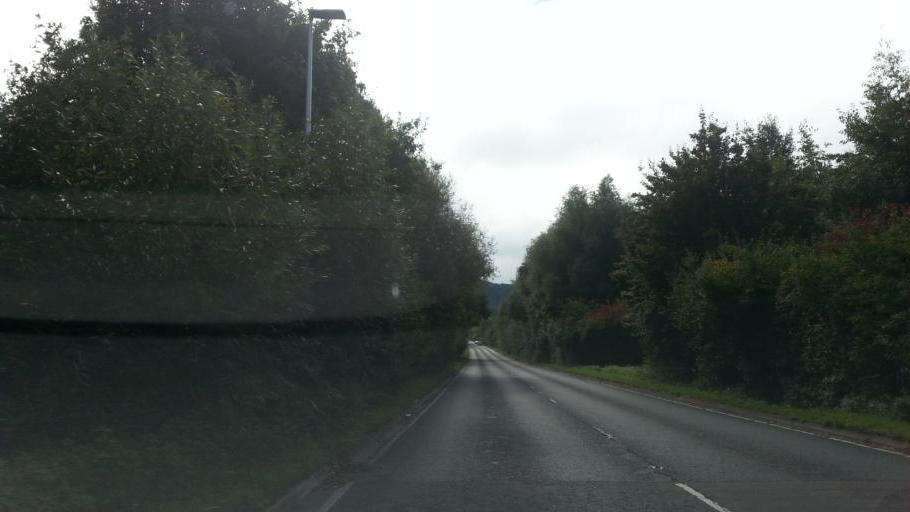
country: GB
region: England
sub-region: Herefordshire
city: Ross on Wye
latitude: 51.9199
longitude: -2.5706
